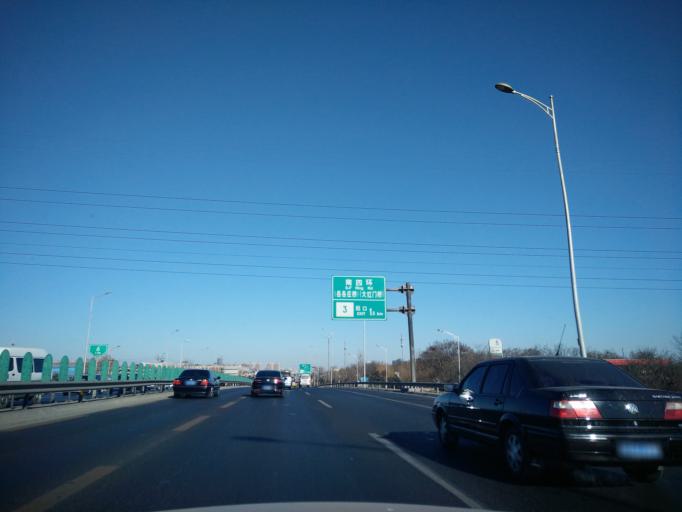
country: CN
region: Beijing
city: Xihongmen
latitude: 39.8123
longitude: 116.3390
